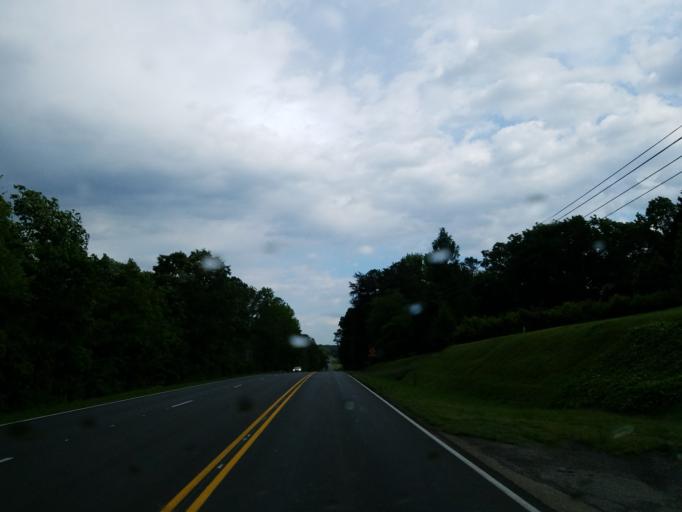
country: US
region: Georgia
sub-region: Pickens County
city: Jasper
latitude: 34.4486
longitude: -84.4032
